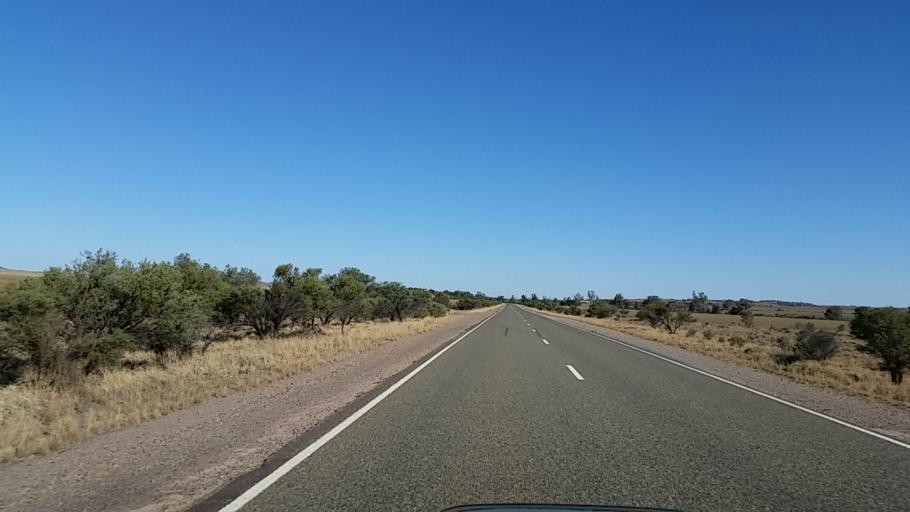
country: AU
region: South Australia
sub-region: Flinders Ranges
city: Quorn
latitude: -32.4661
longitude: 138.5387
